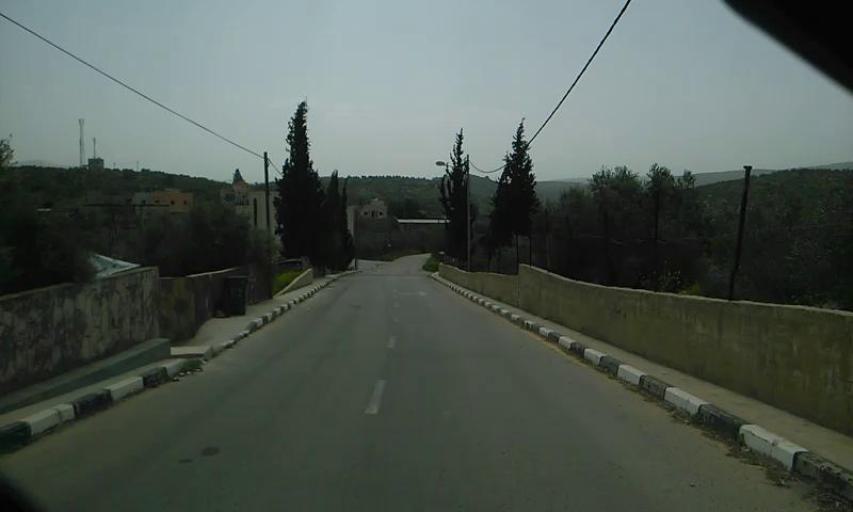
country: PS
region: West Bank
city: Silat al Harithiyah
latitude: 32.5182
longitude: 35.2183
